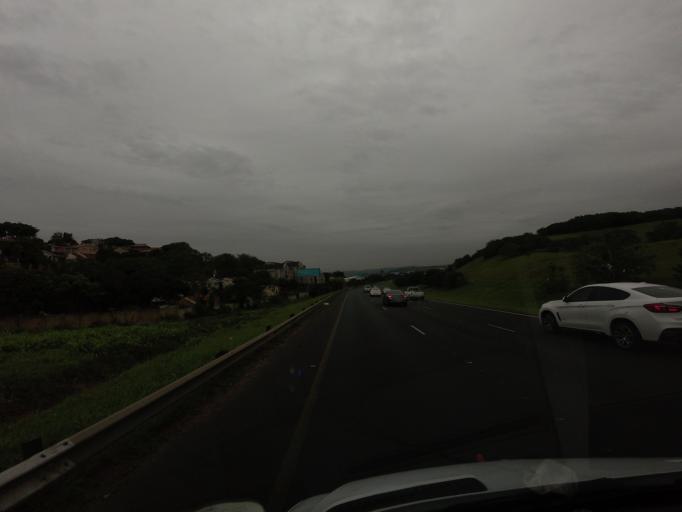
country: ZA
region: KwaZulu-Natal
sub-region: eThekwini Metropolitan Municipality
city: Durban
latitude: -29.7462
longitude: 31.0378
